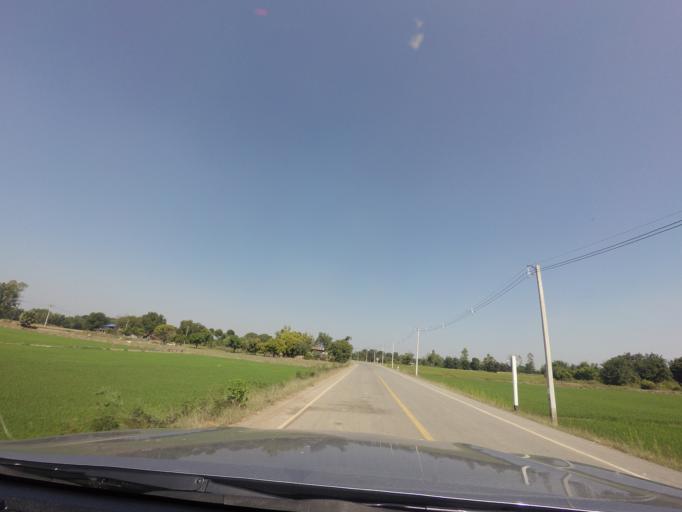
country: TH
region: Sukhothai
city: Si Samrong
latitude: 17.1514
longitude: 99.7699
